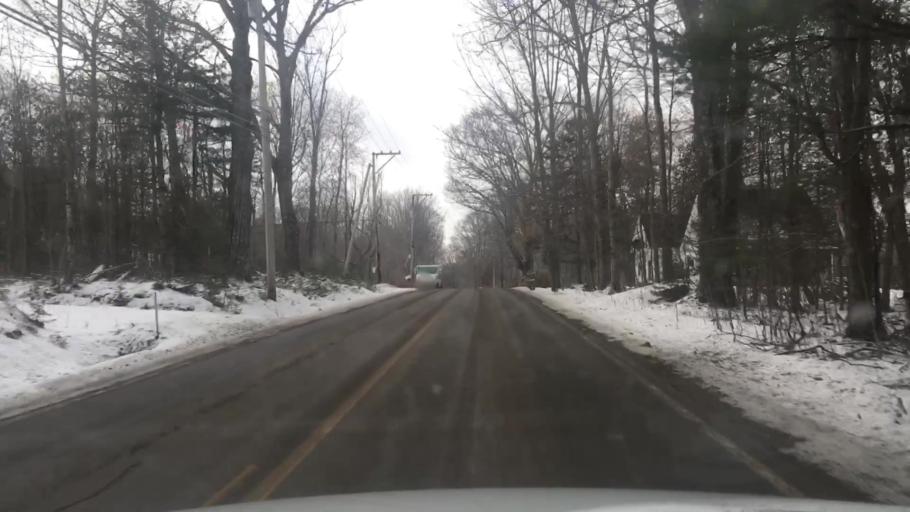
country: US
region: Maine
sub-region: Waldo County
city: Lincolnville
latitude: 44.2917
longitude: -69.0763
